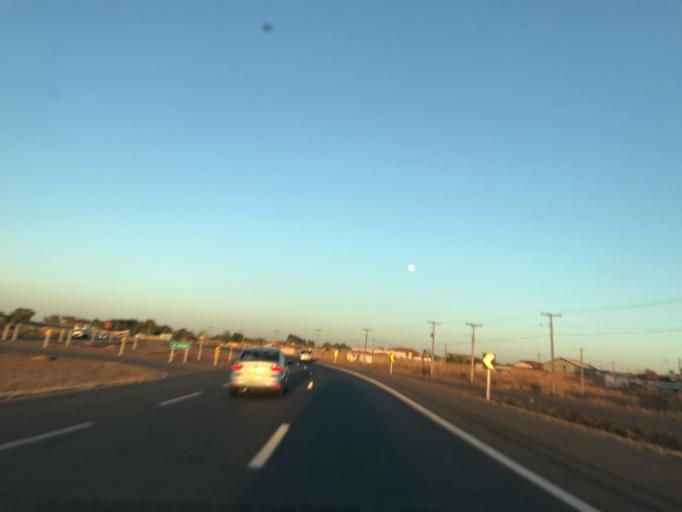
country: BR
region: Goias
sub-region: Abadiania
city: Abadiania
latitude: -16.1874
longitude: -48.7192
